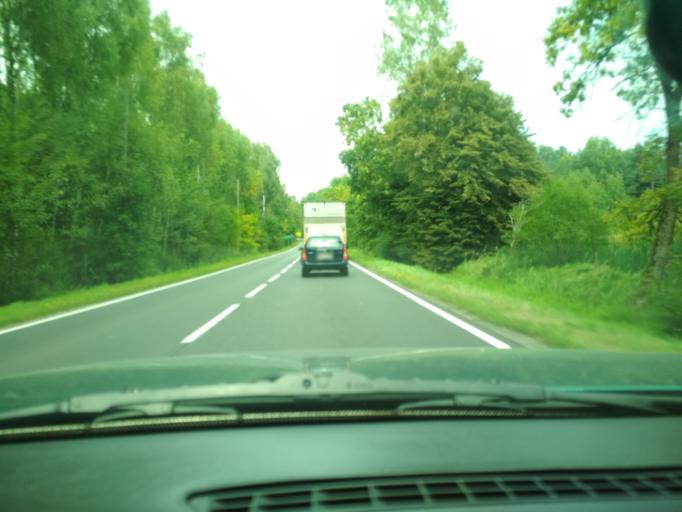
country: PL
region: Silesian Voivodeship
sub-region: Powiat zawiercianski
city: Zawiercie
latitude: 50.4670
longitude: 19.3997
